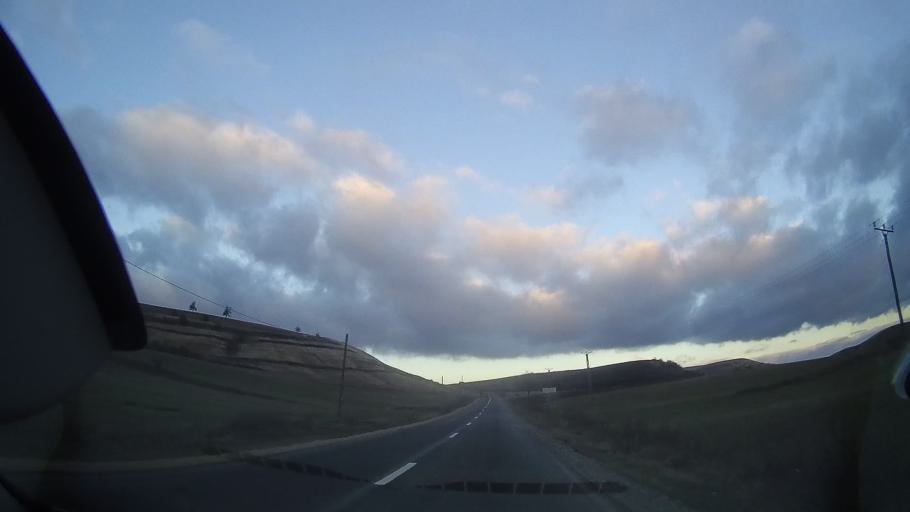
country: RO
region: Cluj
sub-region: Comuna Izvoru Crisului
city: Izvoru Crisului
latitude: 46.8070
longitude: 23.1164
